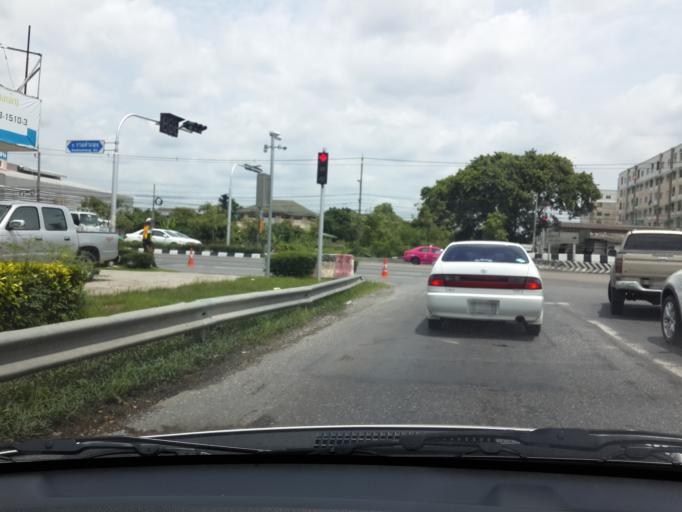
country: TH
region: Bangkok
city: Saphan Sung
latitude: 13.7818
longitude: 100.6829
